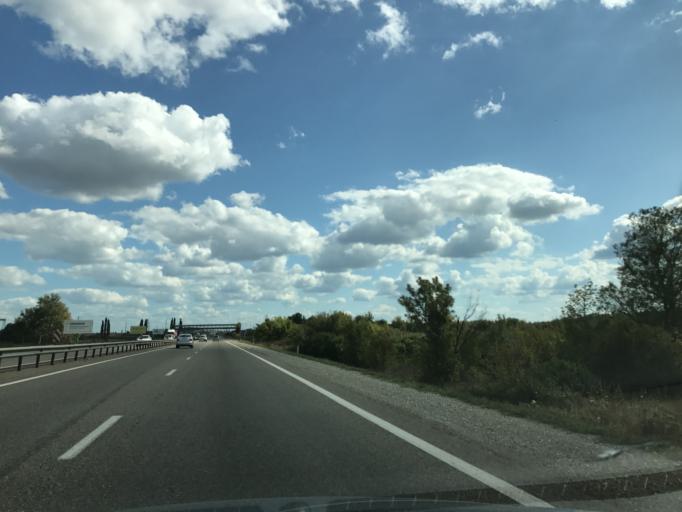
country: RU
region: Adygeya
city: Adygeysk
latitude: 44.9171
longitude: 39.1481
